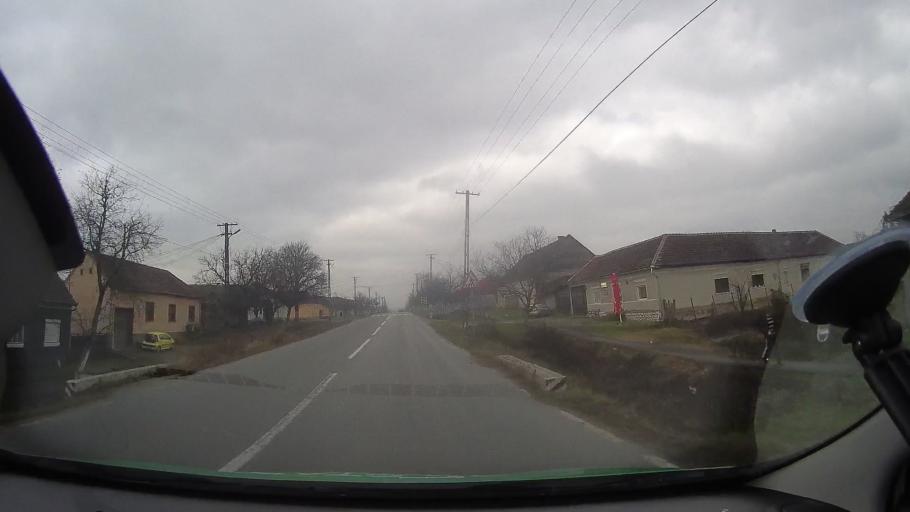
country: RO
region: Arad
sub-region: Comuna Almas
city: Almas
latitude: 46.2878
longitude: 22.2285
